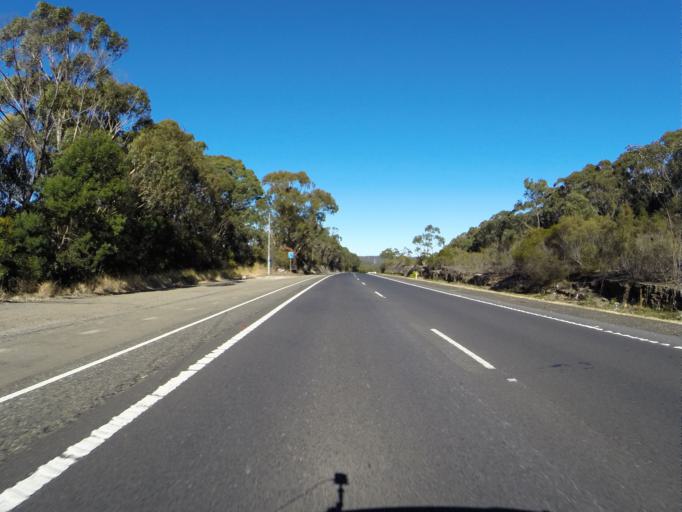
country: AU
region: New South Wales
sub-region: Wollongong
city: Helensburgh
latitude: -34.1774
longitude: 150.9764
